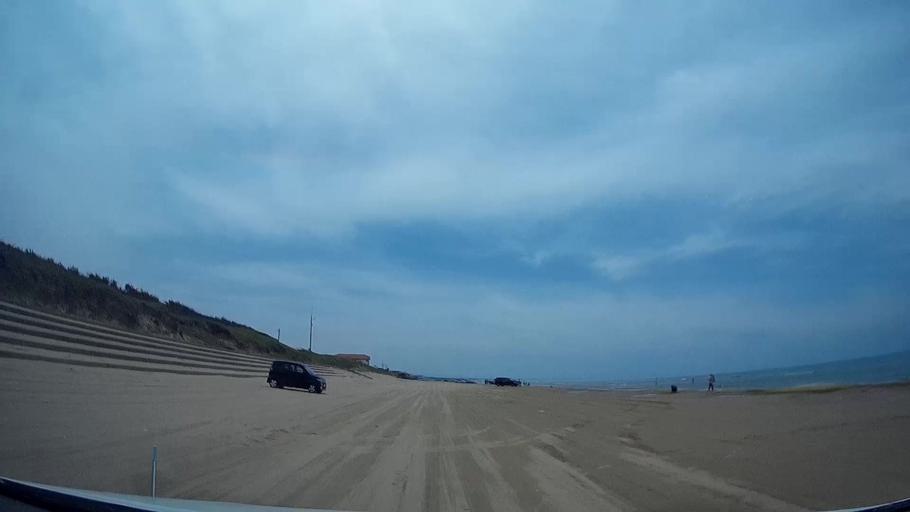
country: JP
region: Ishikawa
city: Hakui
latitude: 36.8965
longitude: 136.7665
